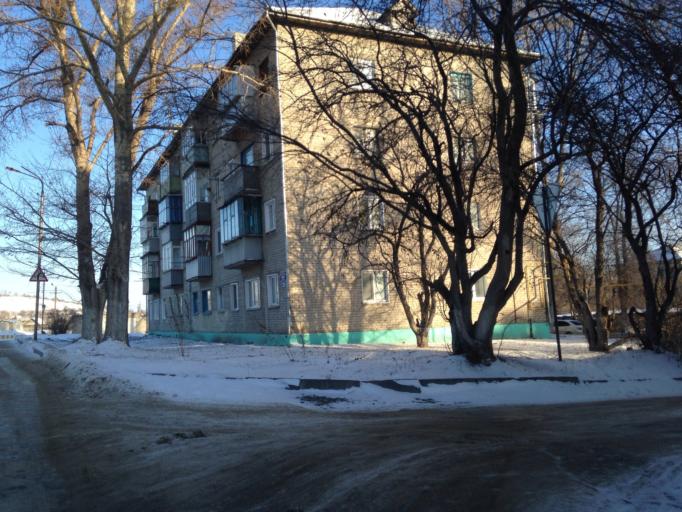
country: RU
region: Ulyanovsk
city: Novoul'yanovsk
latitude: 54.1524
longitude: 48.3780
